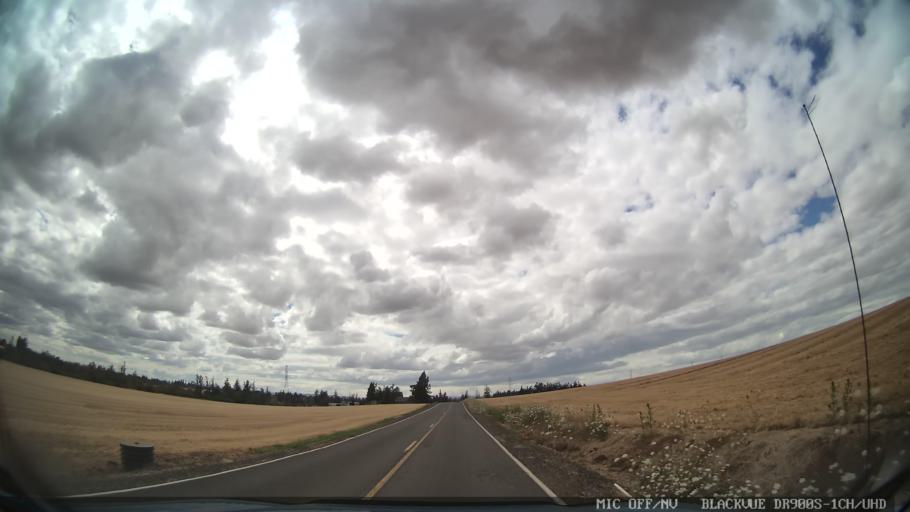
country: US
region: Oregon
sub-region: Marion County
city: Sublimity
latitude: 44.8443
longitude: -122.7626
